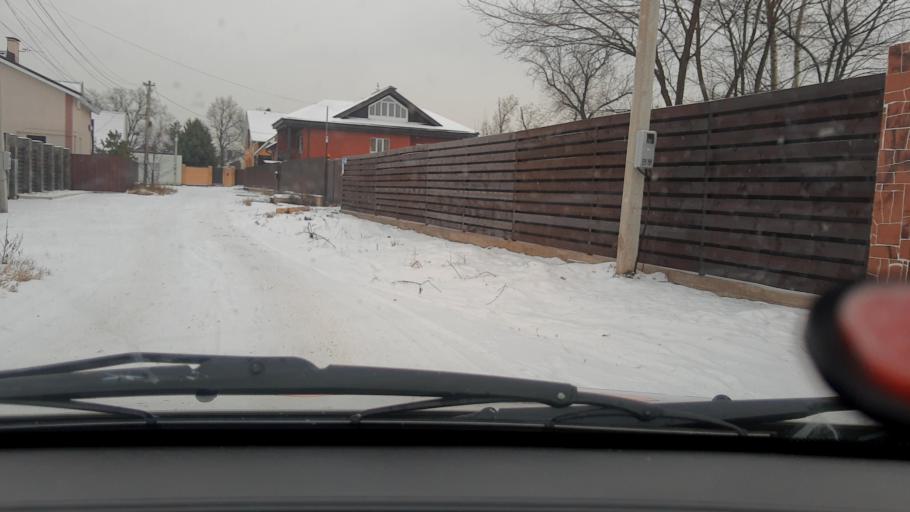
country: RU
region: Bashkortostan
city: Ufa
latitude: 54.7695
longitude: 55.9458
